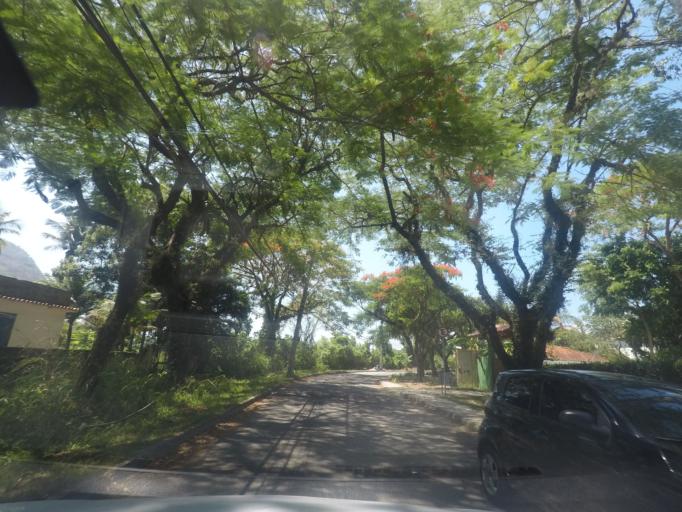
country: BR
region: Rio de Janeiro
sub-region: Nilopolis
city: Nilopolis
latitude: -22.9833
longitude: -43.4590
